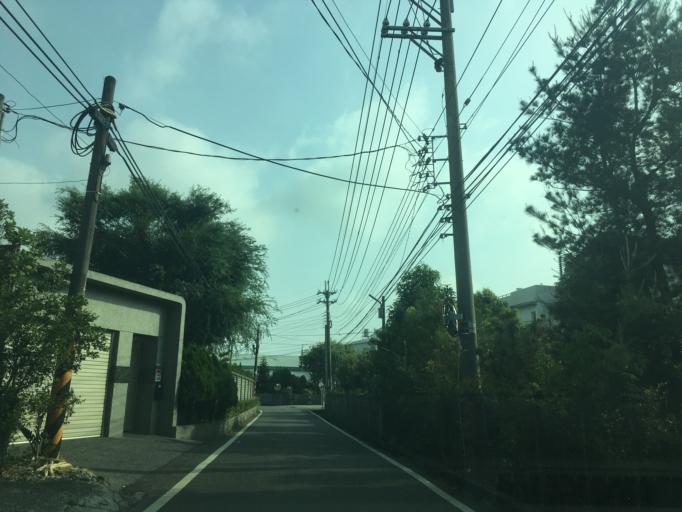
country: TW
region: Taiwan
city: Fengyuan
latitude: 24.2375
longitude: 120.7305
